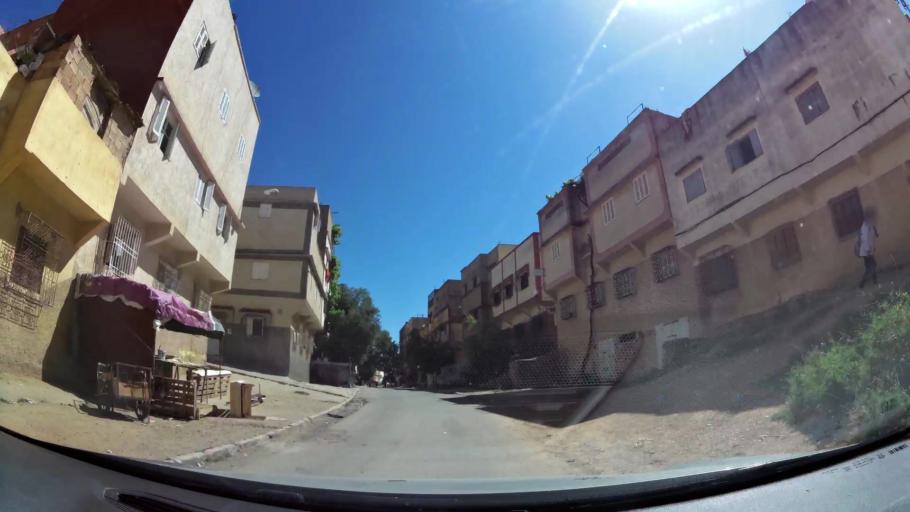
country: MA
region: Meknes-Tafilalet
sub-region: Meknes
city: Meknes
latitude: 33.9105
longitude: -5.5291
